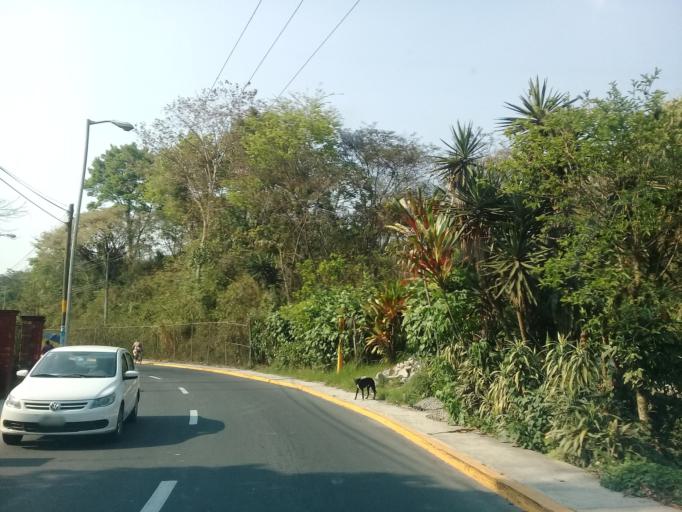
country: MX
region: Veracruz
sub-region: Ixtaczoquitlan
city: Campo Chico
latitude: 18.8497
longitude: -97.0366
